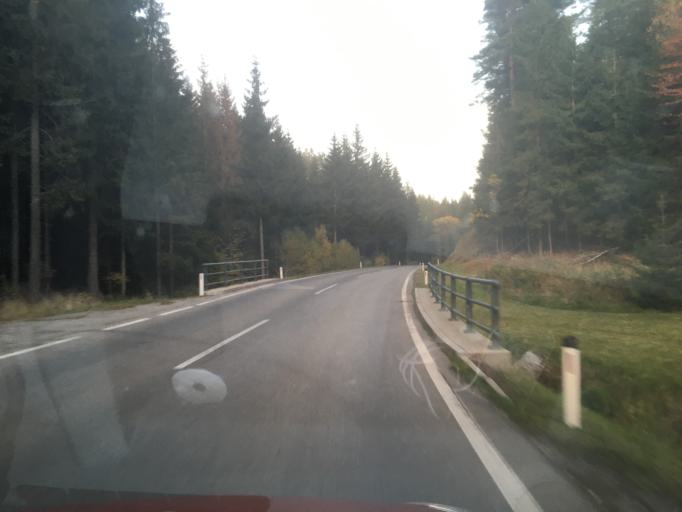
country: AT
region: Lower Austria
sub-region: Politischer Bezirk Zwettl
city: Langschlag
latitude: 48.5796
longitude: 14.8654
